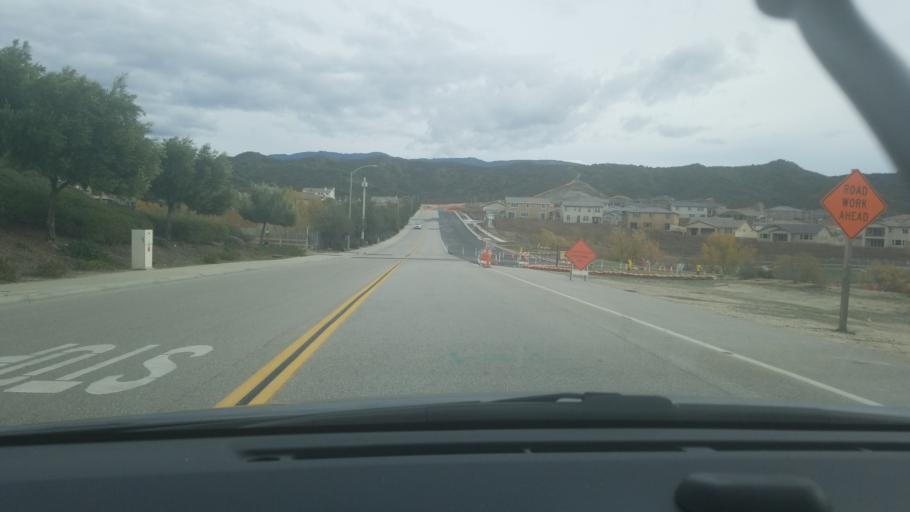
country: US
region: California
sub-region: Riverside County
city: Temecula
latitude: 33.4668
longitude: -117.0705
